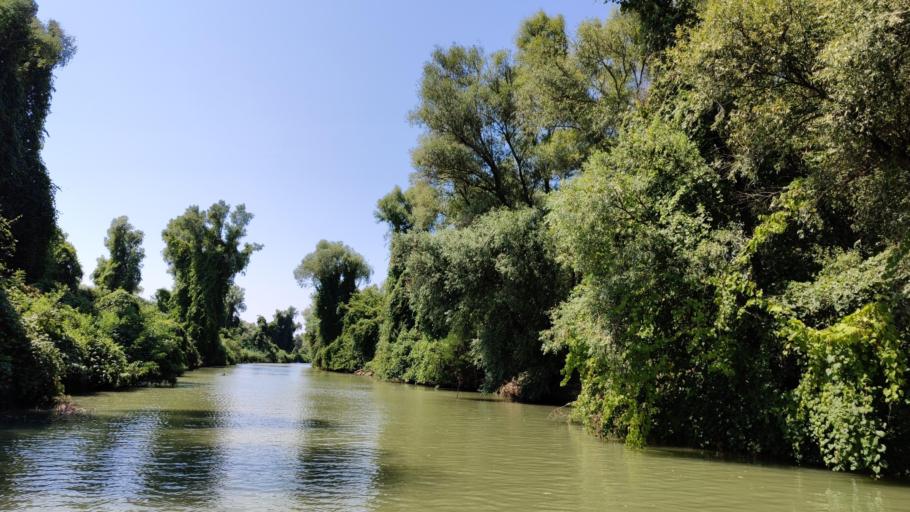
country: RO
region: Tulcea
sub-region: Comuna Pardina
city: Pardina
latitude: 45.2557
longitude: 28.9406
